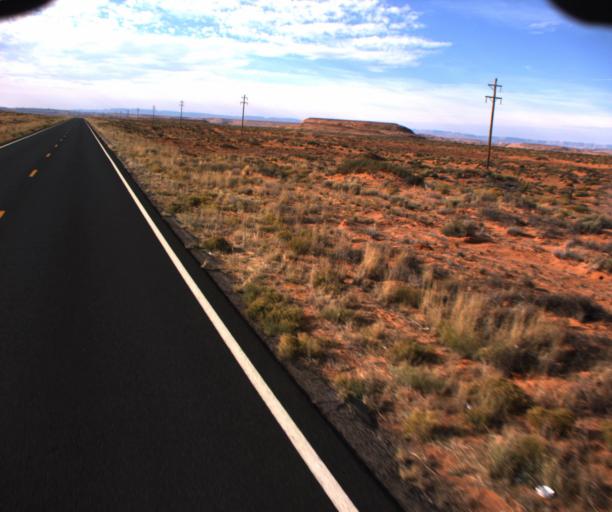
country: US
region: Arizona
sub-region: Apache County
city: Many Farms
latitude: 36.8477
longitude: -109.6394
